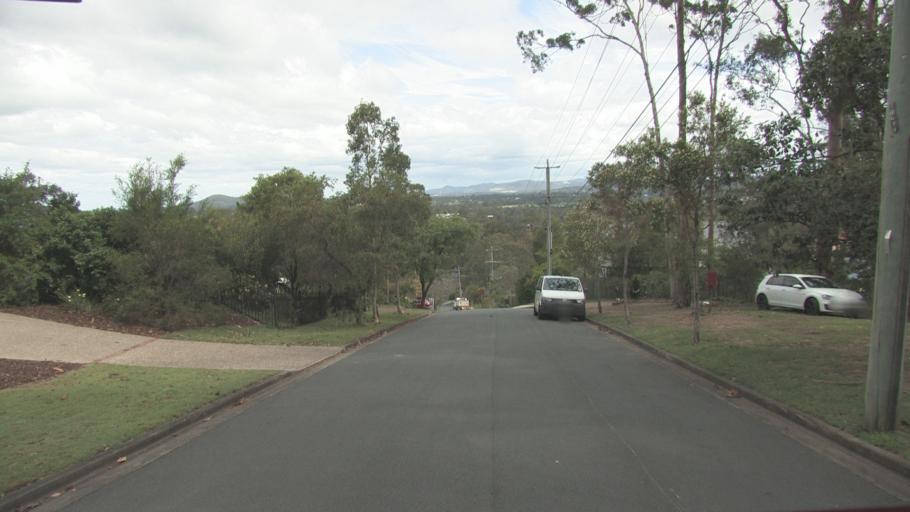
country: AU
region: Queensland
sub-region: Logan
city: Beenleigh
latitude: -27.6642
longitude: 153.1975
